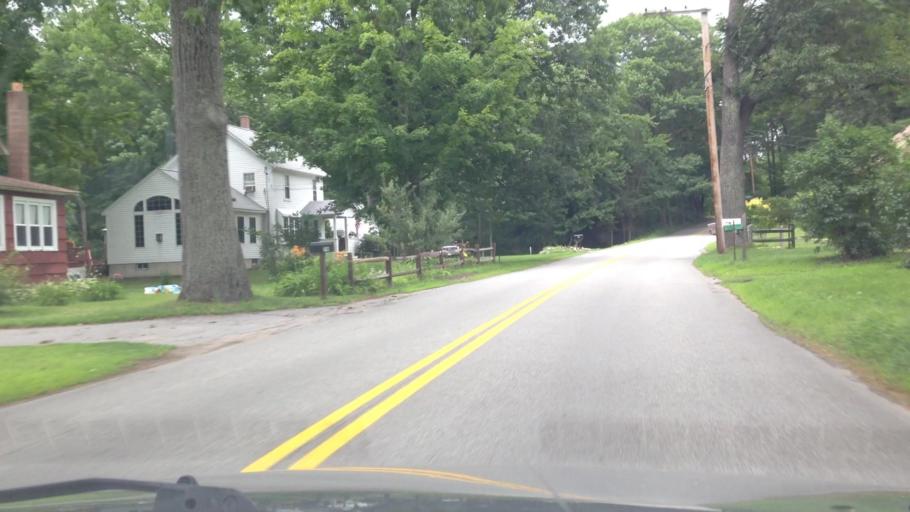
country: US
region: New Hampshire
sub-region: Cheshire County
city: Keene
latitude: 42.9120
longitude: -72.2536
